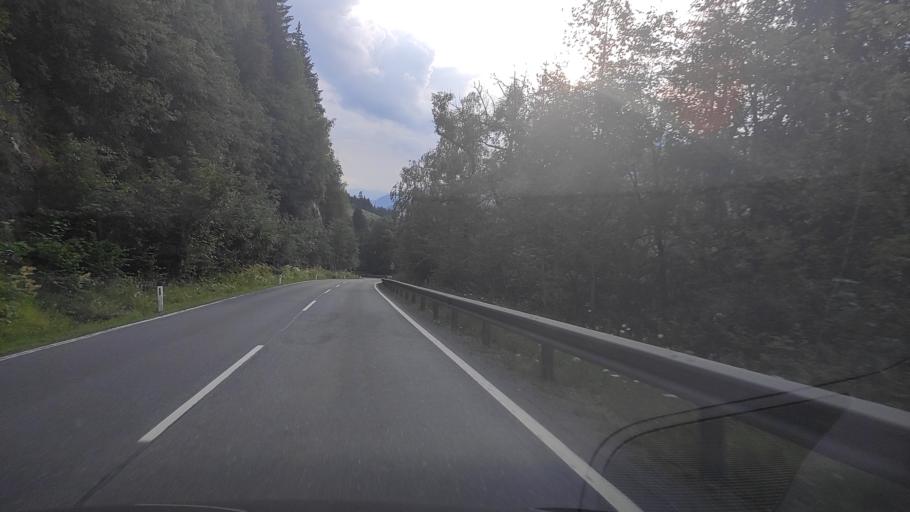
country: AT
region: Salzburg
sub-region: Politischer Bezirk Zell am See
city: Taxenbach
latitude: 47.2851
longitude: 12.9633
